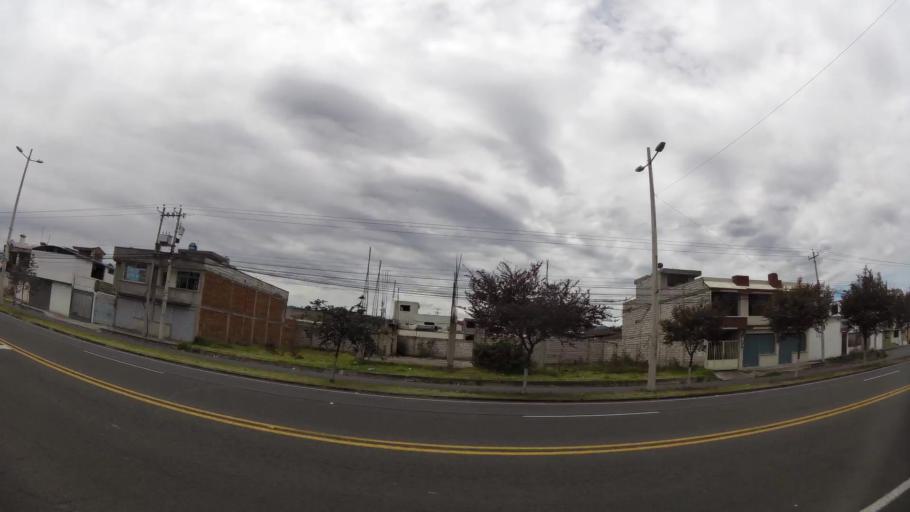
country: EC
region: Cotopaxi
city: Latacunga
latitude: -0.9675
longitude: -78.6100
